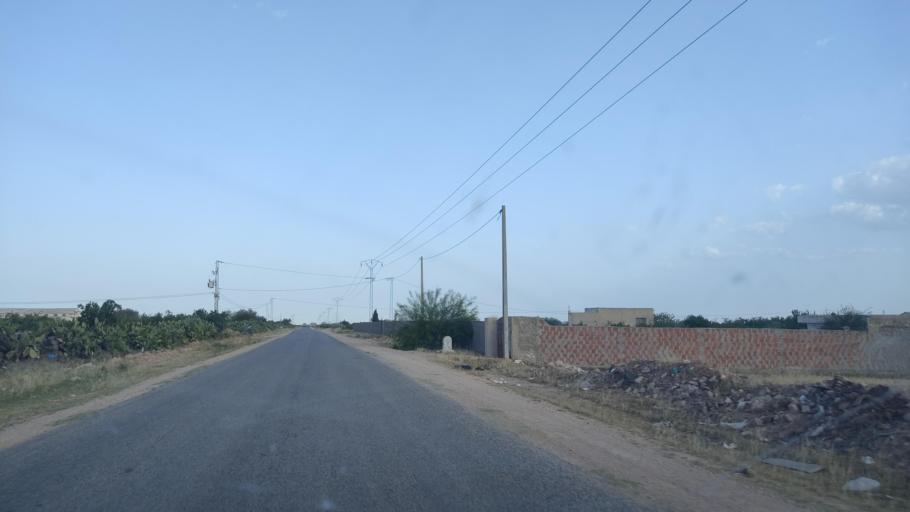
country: TN
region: Safaqis
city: Sfax
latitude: 34.8226
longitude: 10.6465
